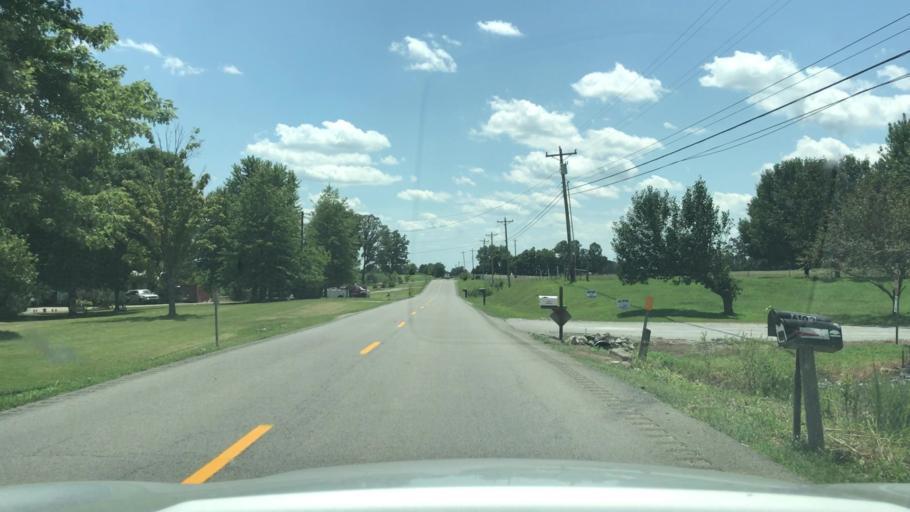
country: US
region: Kentucky
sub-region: Christian County
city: Hopkinsville
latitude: 36.9250
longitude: -87.4345
